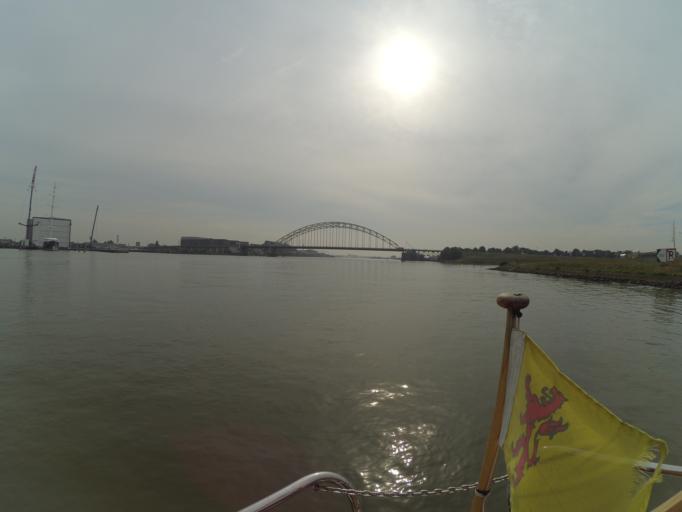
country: NL
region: South Holland
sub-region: Gemeente Alblasserdam
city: Alblasserdam
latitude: 51.8591
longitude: 4.6506
